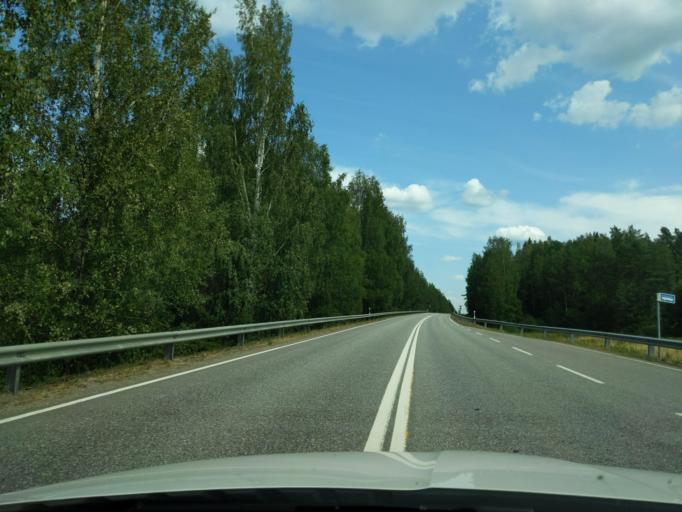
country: FI
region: Haeme
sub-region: Haemeenlinna
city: Lammi
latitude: 61.1298
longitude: 24.9672
